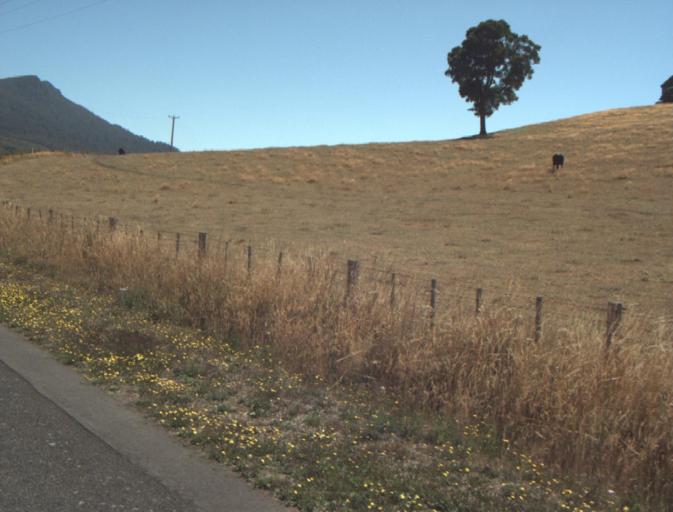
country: AU
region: Tasmania
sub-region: Launceston
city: Newstead
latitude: -41.3469
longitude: 147.3031
